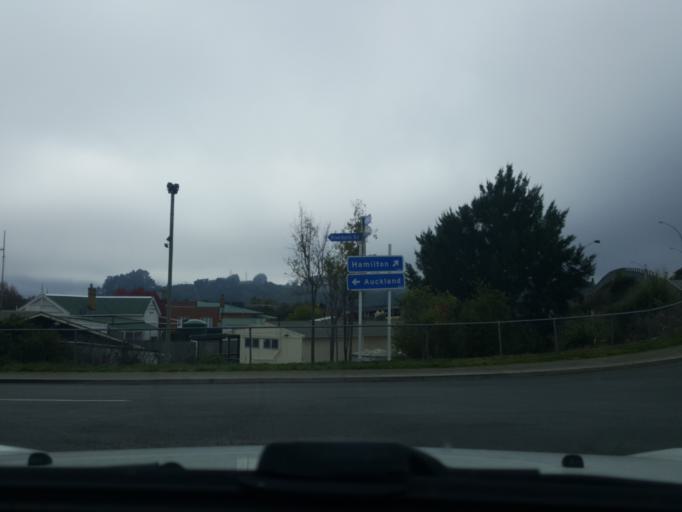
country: NZ
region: Auckland
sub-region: Auckland
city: Pukekohe East
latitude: -37.2805
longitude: 175.0470
